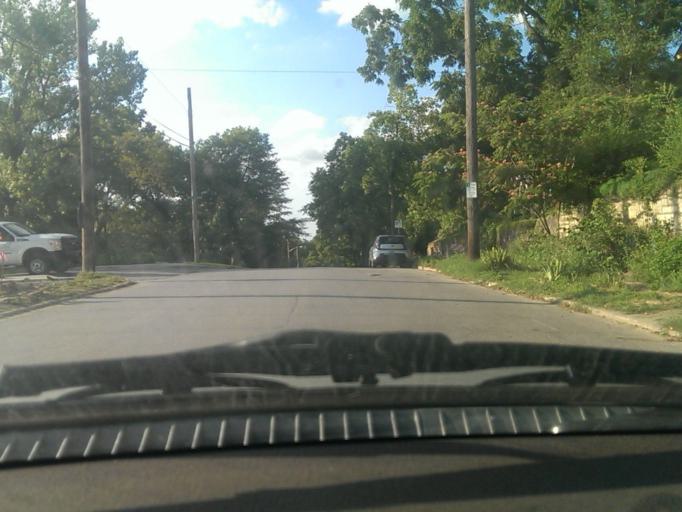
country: US
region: Kansas
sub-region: Johnson County
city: Westwood
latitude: 39.0617
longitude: -94.6072
